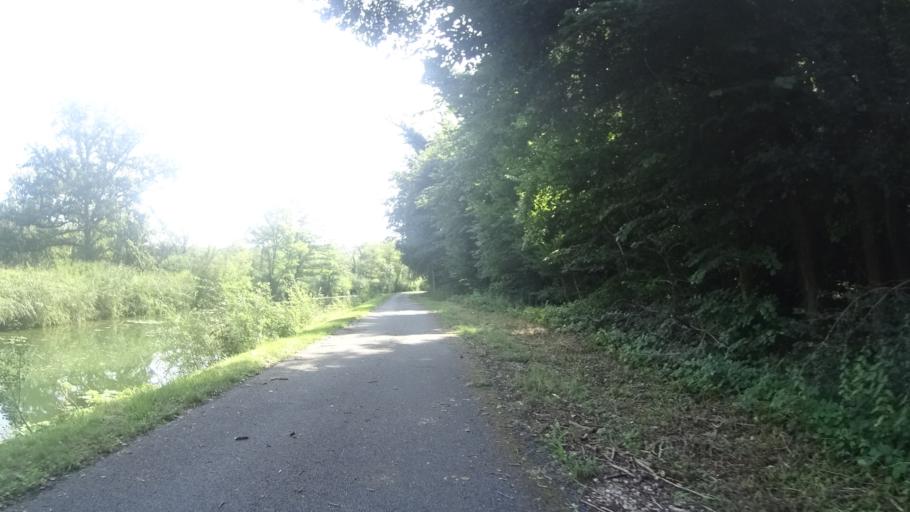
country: FR
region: Franche-Comte
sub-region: Departement du Doubs
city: Clerval
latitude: 47.4247
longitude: 6.5513
